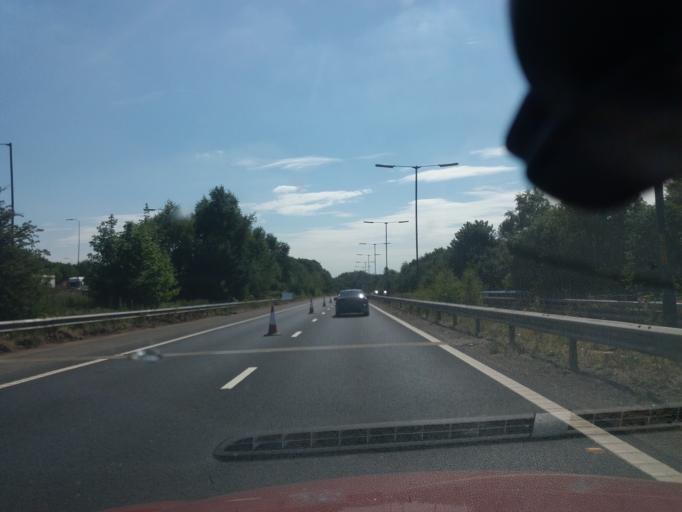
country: GB
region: England
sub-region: Borough of Bolton
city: Kearsley
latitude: 53.5200
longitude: -2.3679
